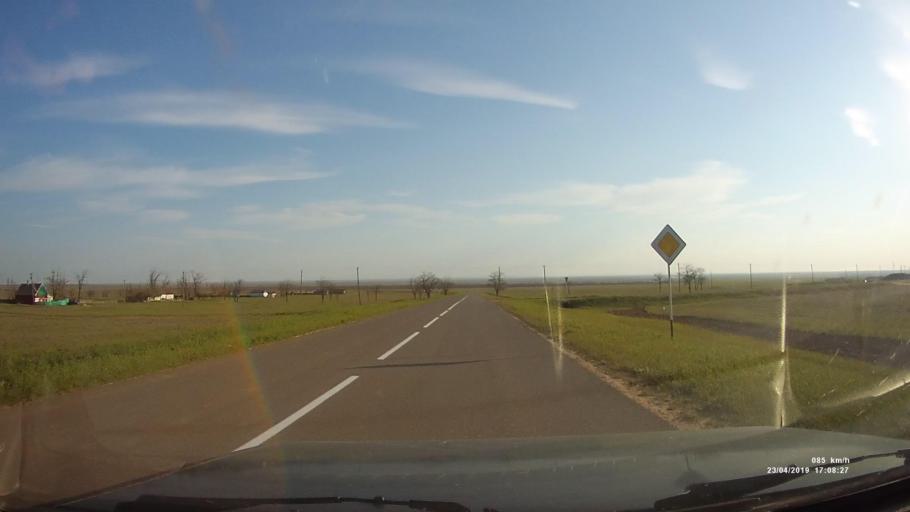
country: RU
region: Kalmykiya
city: Priyutnoye
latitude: 46.2714
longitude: 43.4877
